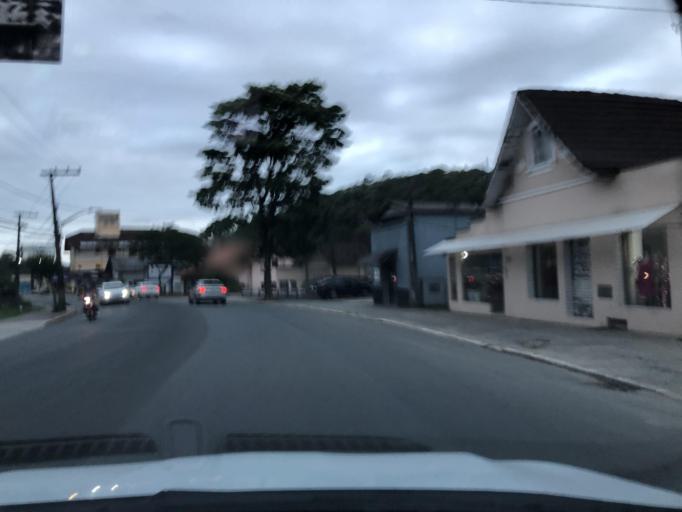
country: BR
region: Santa Catarina
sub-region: Joinville
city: Joinville
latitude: -26.2966
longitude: -48.8723
